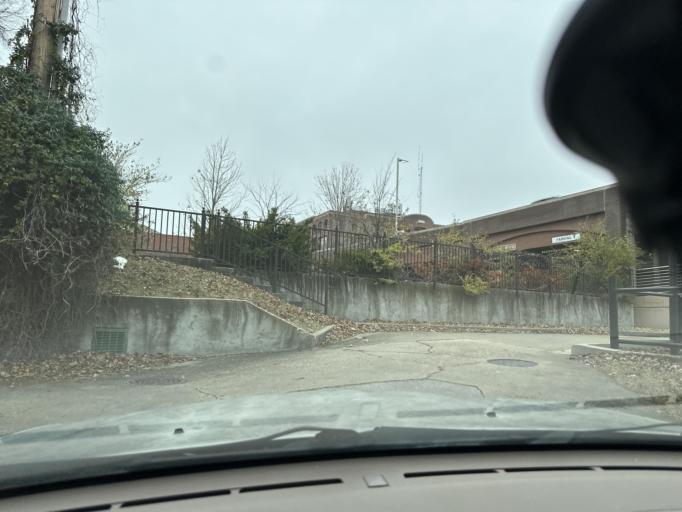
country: US
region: Arkansas
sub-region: Washington County
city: Fayetteville
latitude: 36.0653
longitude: -94.1562
